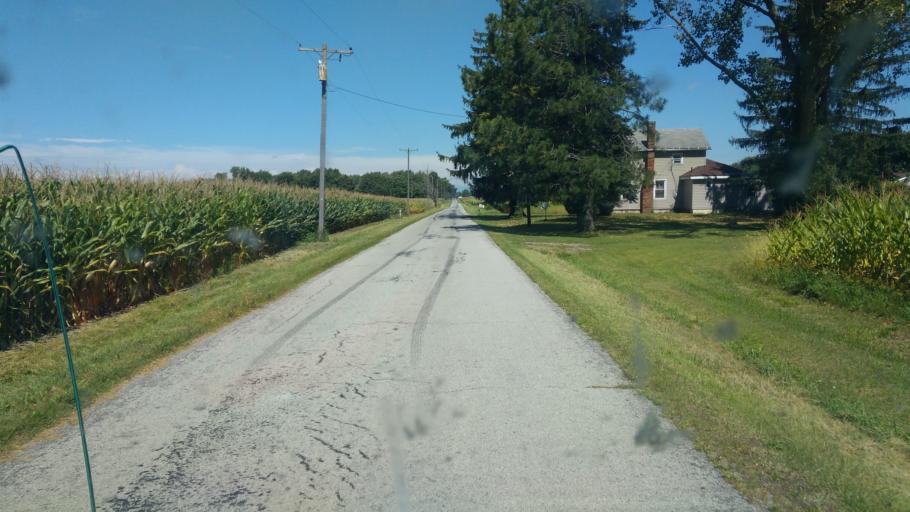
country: US
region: Ohio
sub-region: Crawford County
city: Galion
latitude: 40.7724
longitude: -82.8728
